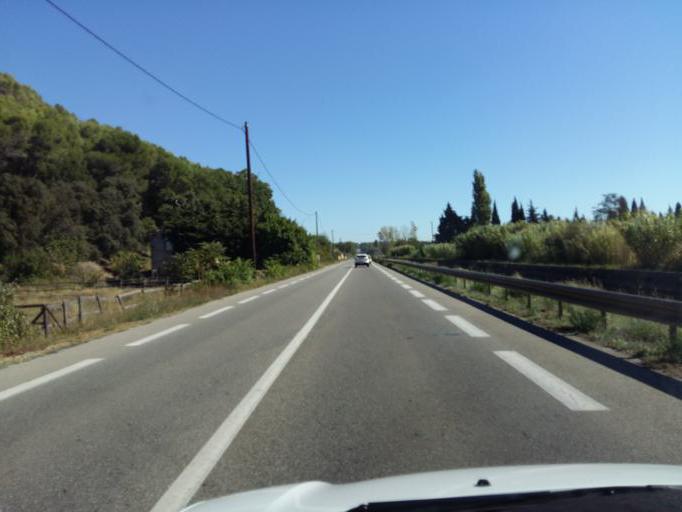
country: FR
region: Provence-Alpes-Cote d'Azur
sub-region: Departement des Bouches-du-Rhone
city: Mallemort
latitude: 43.7553
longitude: 5.1637
